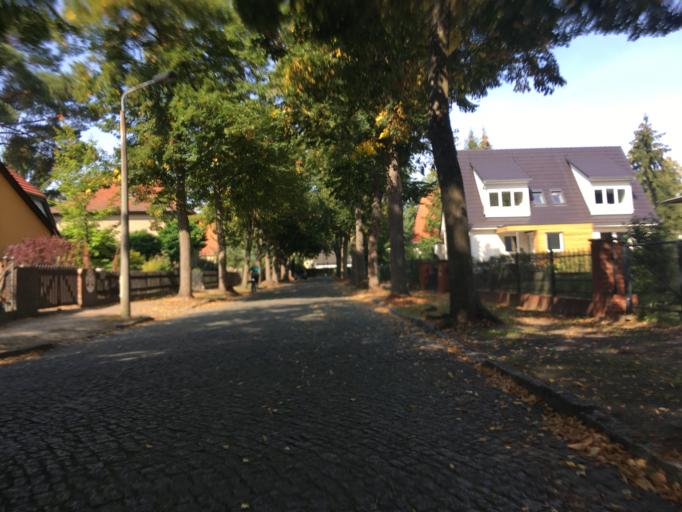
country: DE
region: Brandenburg
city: Zeuthen
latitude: 52.3677
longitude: 13.6304
